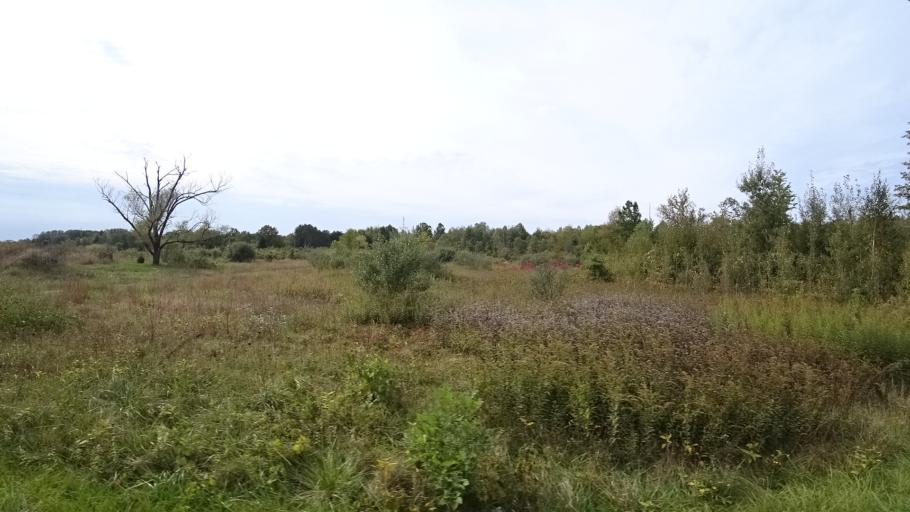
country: US
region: Indiana
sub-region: LaPorte County
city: Trail Creek
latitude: 41.7126
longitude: -86.8163
